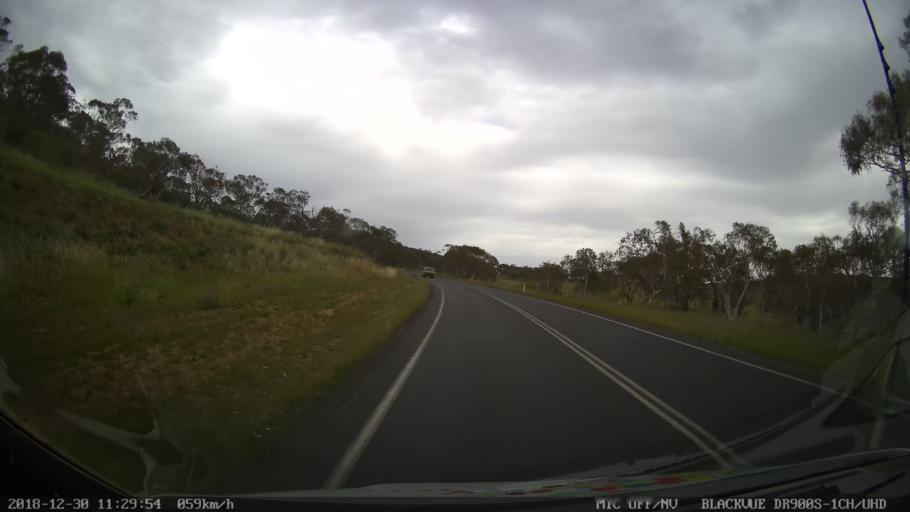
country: AU
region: New South Wales
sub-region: Snowy River
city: Jindabyne
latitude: -36.4465
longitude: 148.6086
